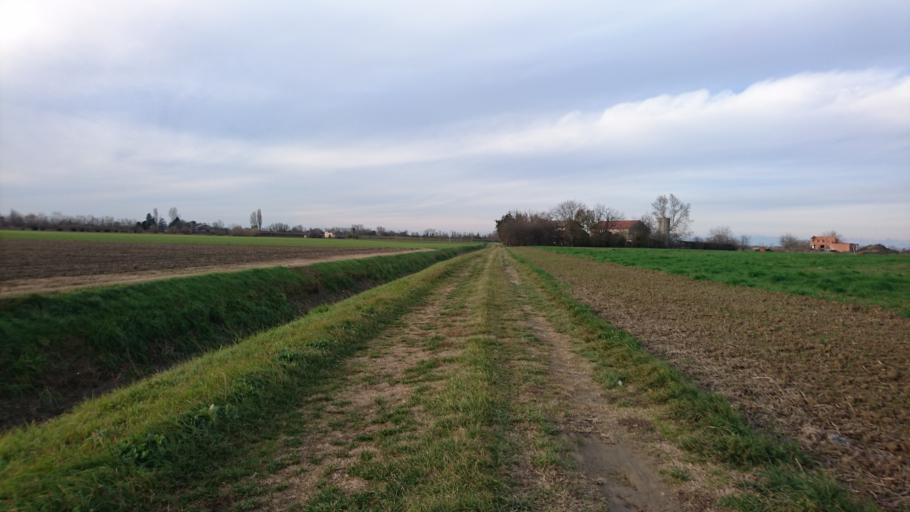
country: IT
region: Veneto
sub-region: Provincia di Padova
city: Polverara
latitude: 45.3231
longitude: 11.9505
